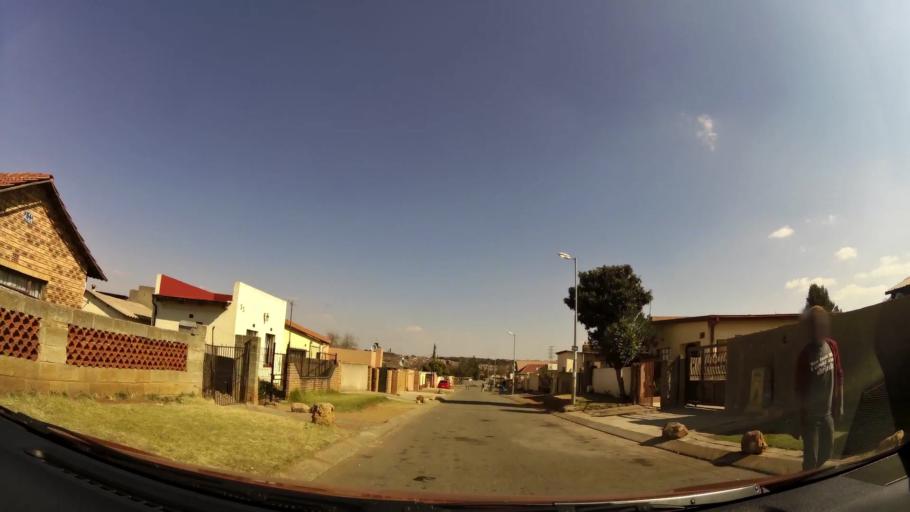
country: ZA
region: Gauteng
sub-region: City of Johannesburg Metropolitan Municipality
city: Soweto
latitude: -26.2350
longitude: 27.8798
